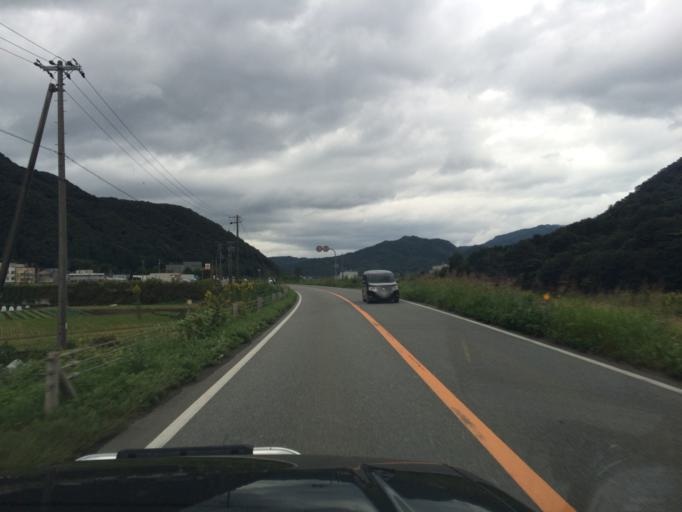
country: JP
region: Hyogo
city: Toyooka
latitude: 35.4110
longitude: 134.7797
